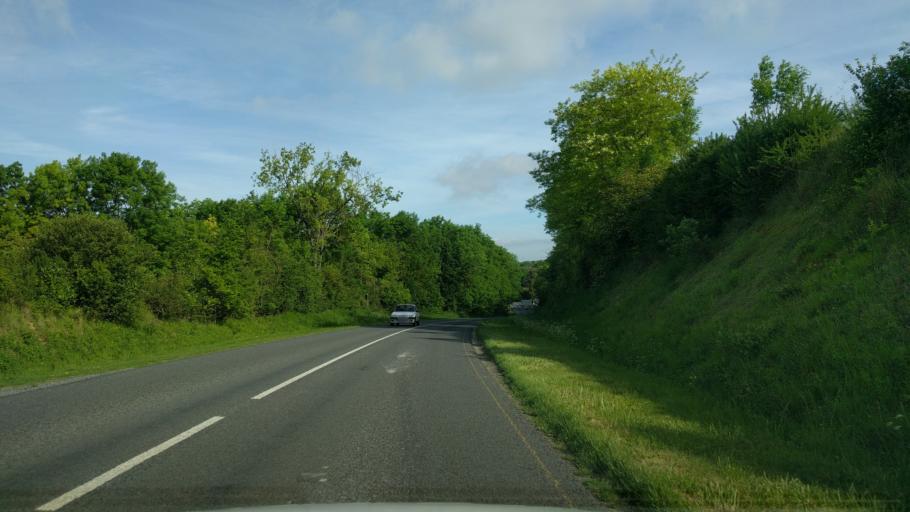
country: FR
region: Picardie
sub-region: Departement de la Somme
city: Peronne
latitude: 49.9511
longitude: 2.8992
